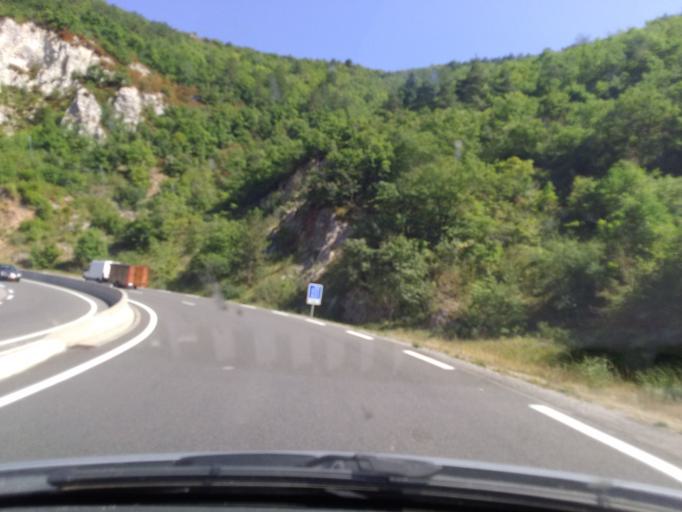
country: FR
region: Midi-Pyrenees
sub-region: Departement de l'Aveyron
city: Millau
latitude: 44.0910
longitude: 3.1141
